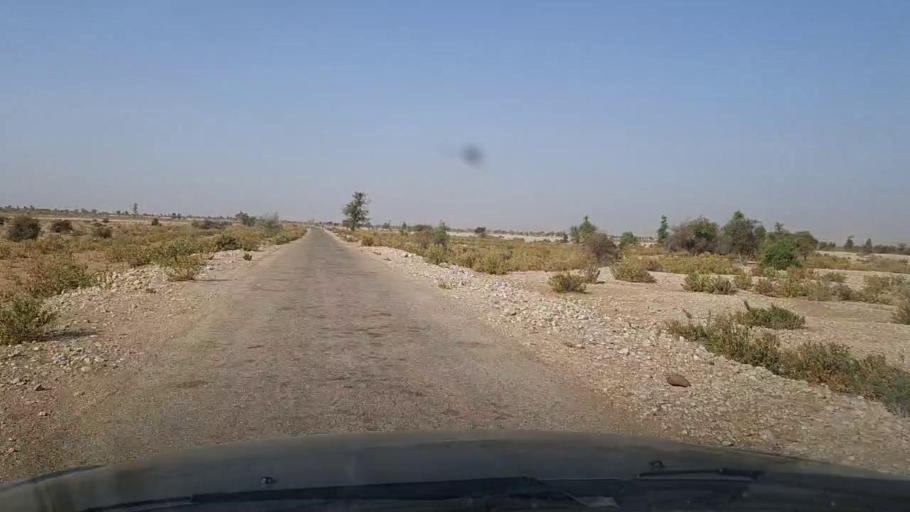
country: PK
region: Sindh
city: Sann
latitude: 25.9358
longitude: 68.0266
